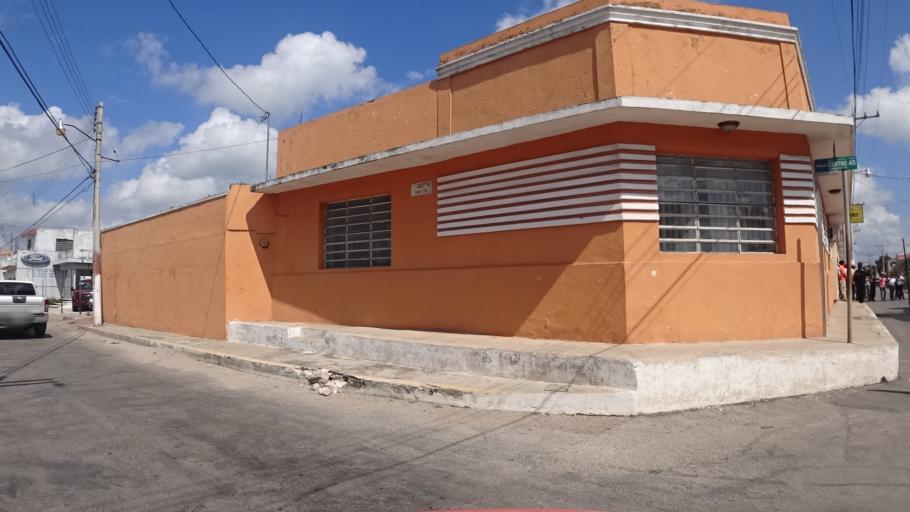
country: MX
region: Yucatan
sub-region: Tizimin
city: Tizimin
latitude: 21.1459
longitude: -88.1512
